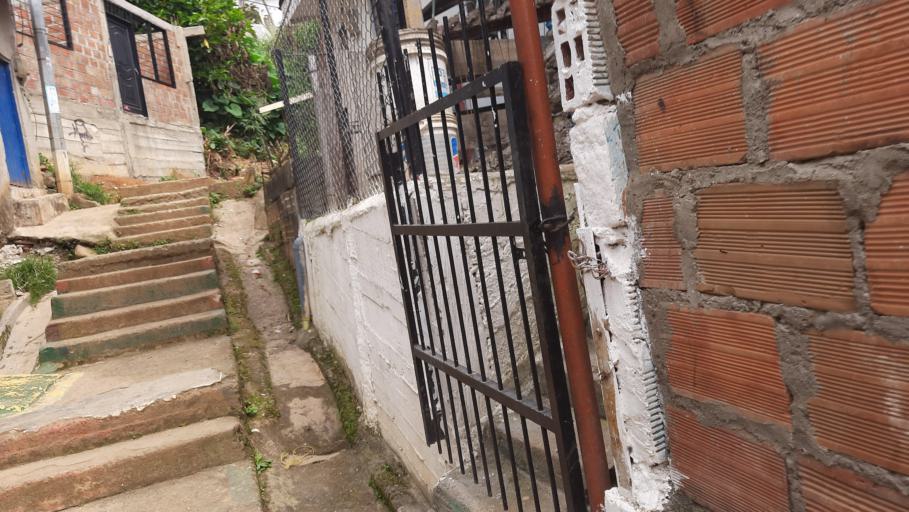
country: CO
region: Valle del Cauca
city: Cali
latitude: 3.3746
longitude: -76.5575
